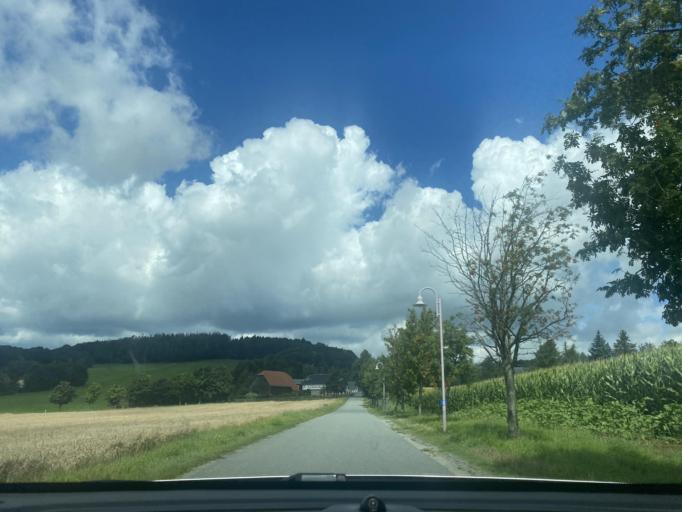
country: DE
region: Saxony
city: Beiersdorf
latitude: 51.0746
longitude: 14.5322
